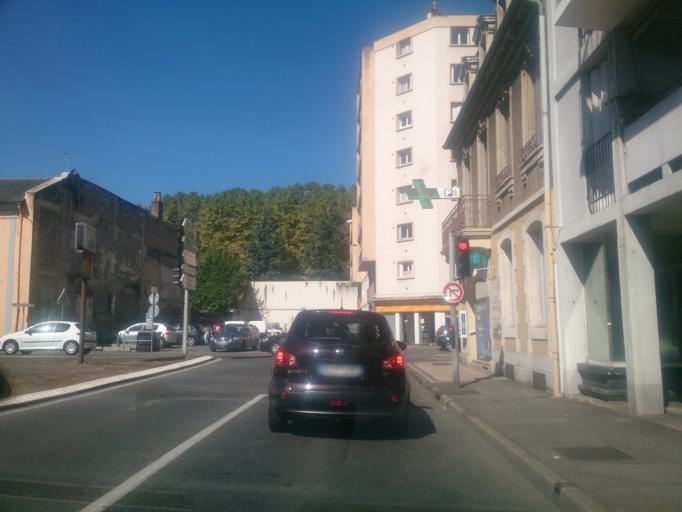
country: FR
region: Midi-Pyrenees
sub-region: Departement des Hautes-Pyrenees
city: Tarbes
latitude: 43.2290
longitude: 0.0705
